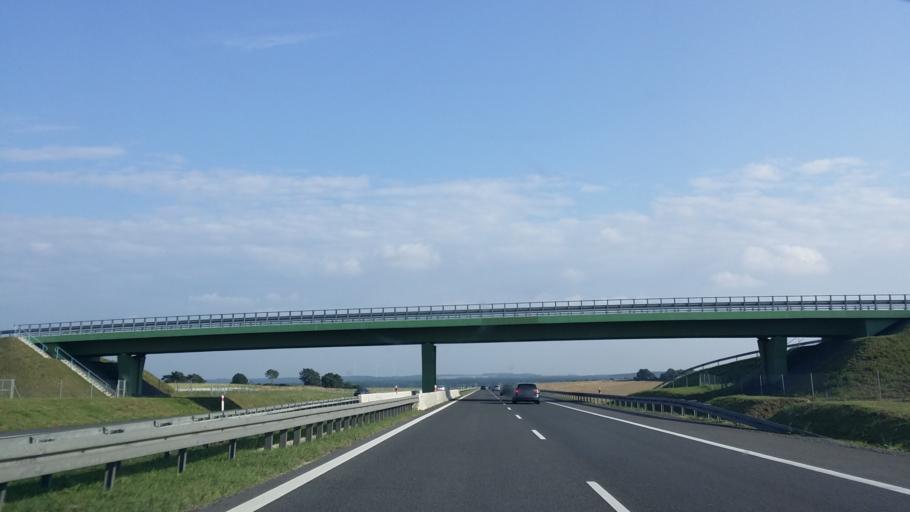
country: PL
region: Lubusz
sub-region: Powiat miedzyrzecki
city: Miedzyrzecz
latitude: 52.3598
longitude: 15.5514
